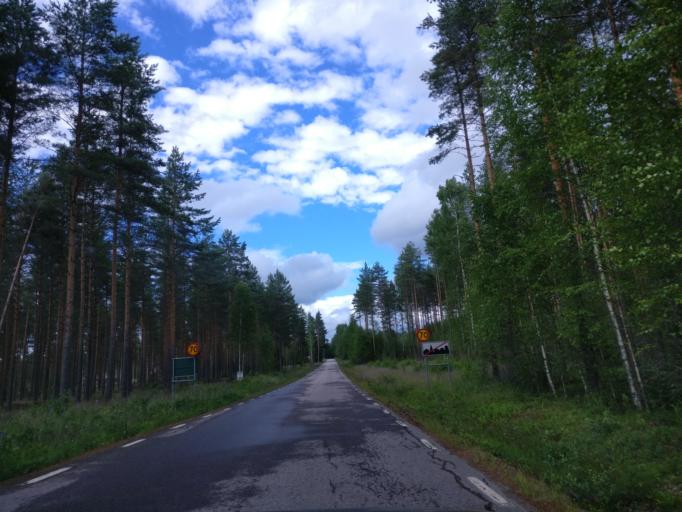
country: SE
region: Vaermland
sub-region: Munkfors Kommun
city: Munkfors
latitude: 59.9768
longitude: 13.4852
